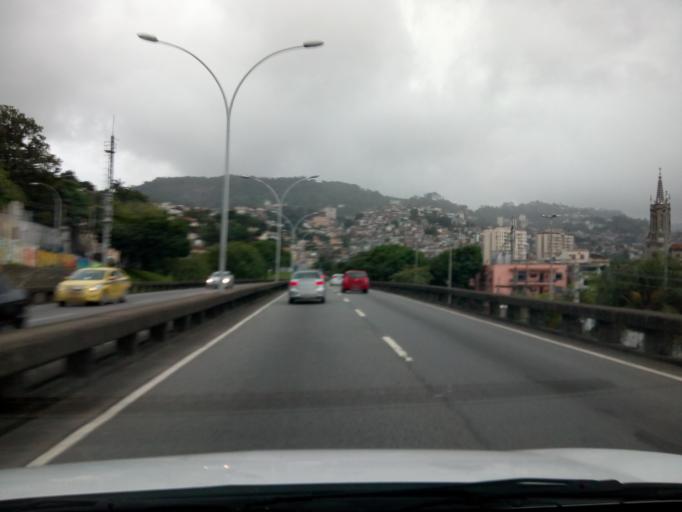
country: BR
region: Rio de Janeiro
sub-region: Rio De Janeiro
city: Rio de Janeiro
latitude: -22.9136
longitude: -43.1952
